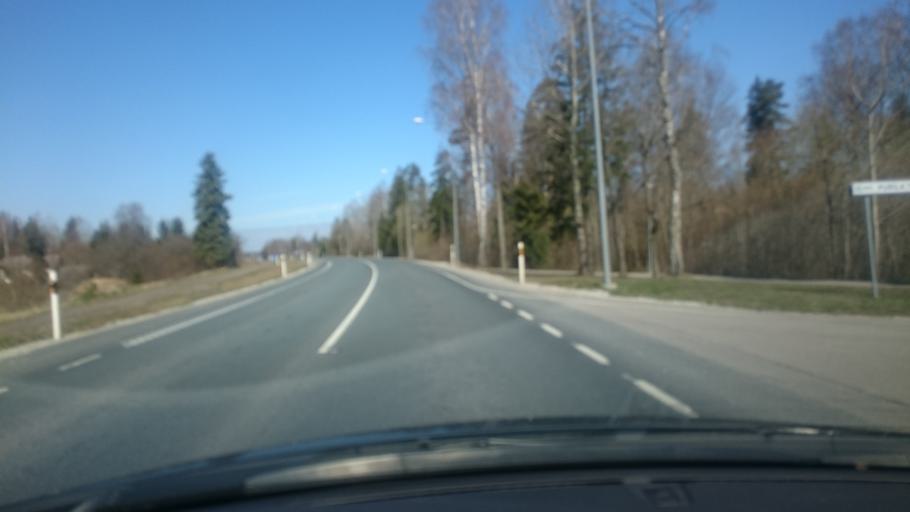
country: EE
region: Raplamaa
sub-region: Rapla vald
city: Rapla
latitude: 59.0675
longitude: 24.8160
